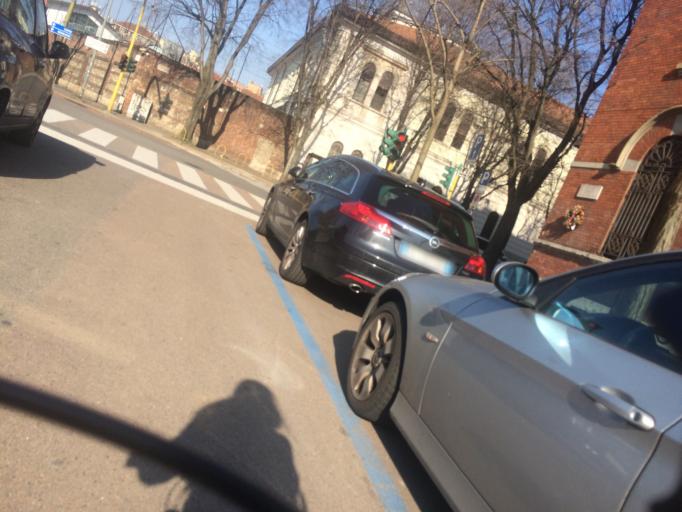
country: IT
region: Lombardy
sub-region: Citta metropolitana di Milano
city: Milano
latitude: 45.4742
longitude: 9.1643
